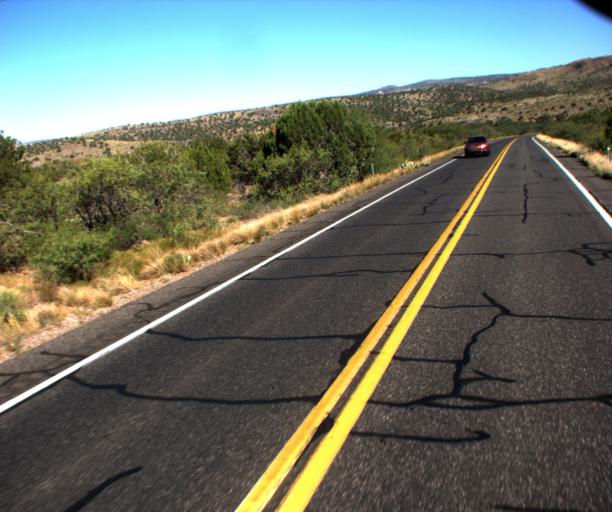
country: US
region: Arizona
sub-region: Yavapai County
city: Big Park
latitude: 34.7110
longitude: -111.7762
